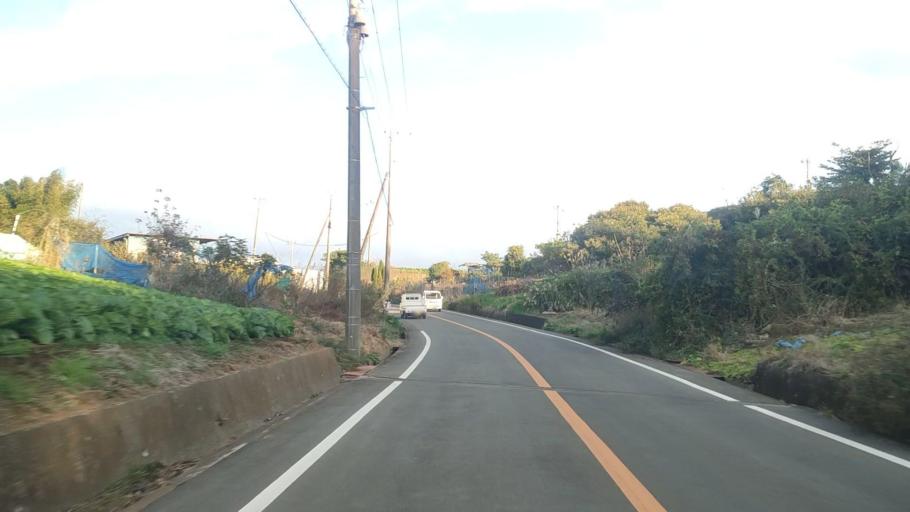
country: JP
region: Shizuoka
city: Mishima
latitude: 35.1336
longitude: 138.9640
